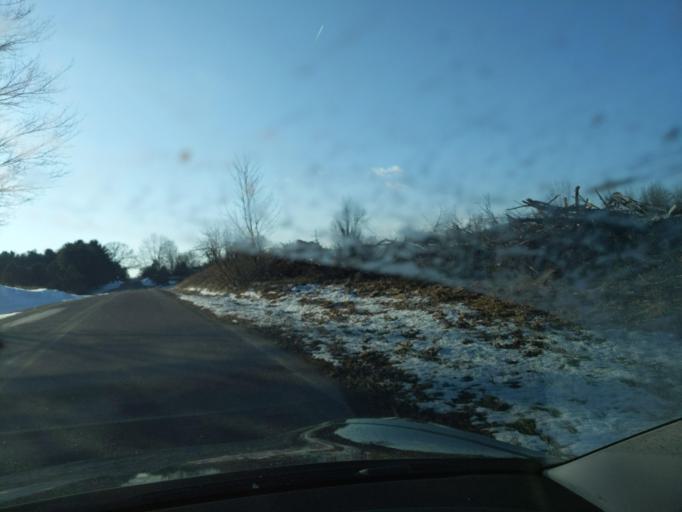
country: US
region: Michigan
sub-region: Ingham County
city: Stockbridge
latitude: 42.5194
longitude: -84.2331
